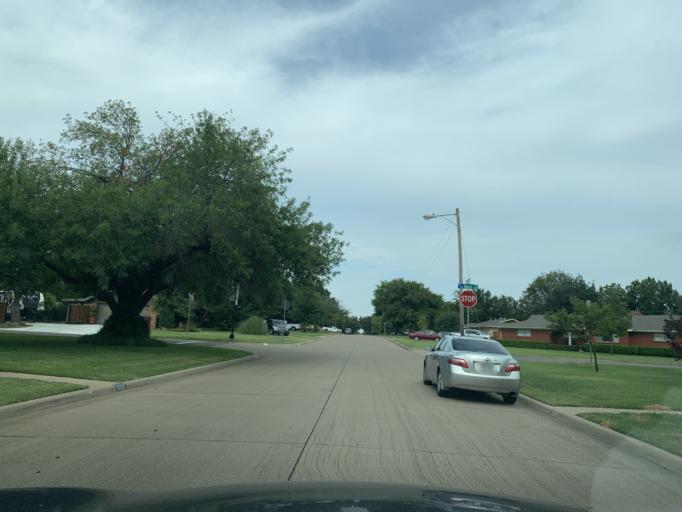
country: US
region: Texas
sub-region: Tarrant County
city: North Richland Hills
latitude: 32.8338
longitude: -97.2335
